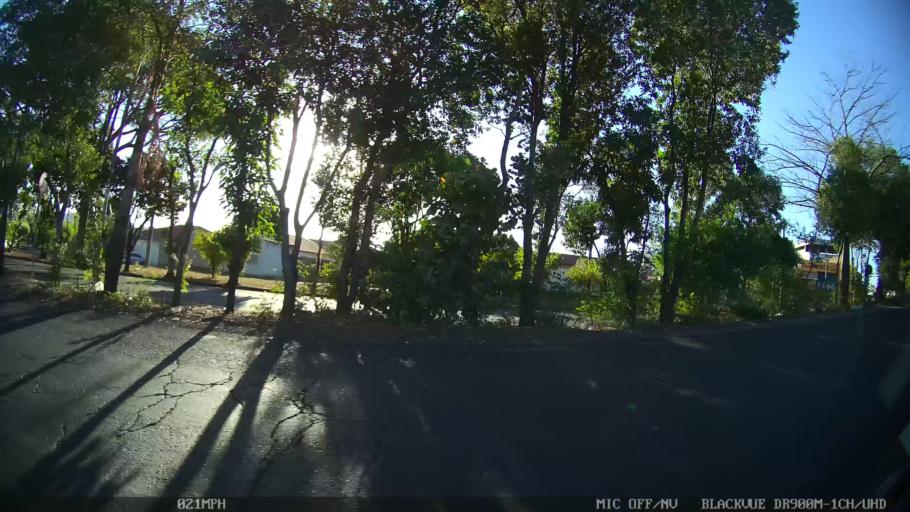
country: BR
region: Sao Paulo
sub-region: Sao Jose Do Rio Preto
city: Sao Jose do Rio Preto
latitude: -20.8017
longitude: -49.3559
